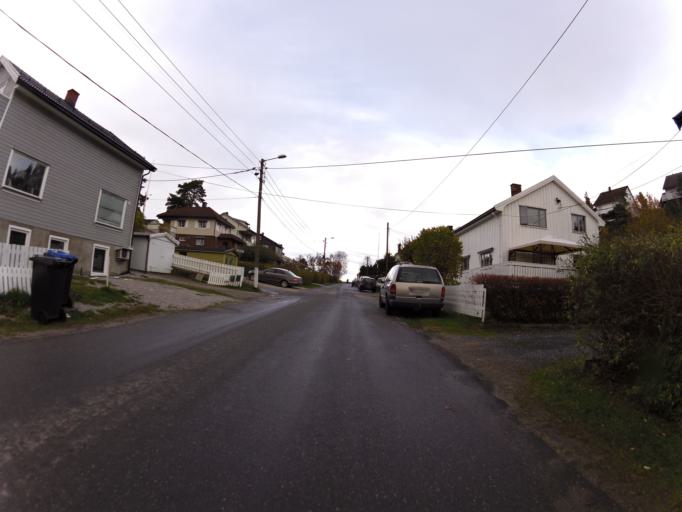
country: NO
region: Ostfold
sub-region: Fredrikstad
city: Fredrikstad
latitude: 59.2303
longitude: 10.9225
